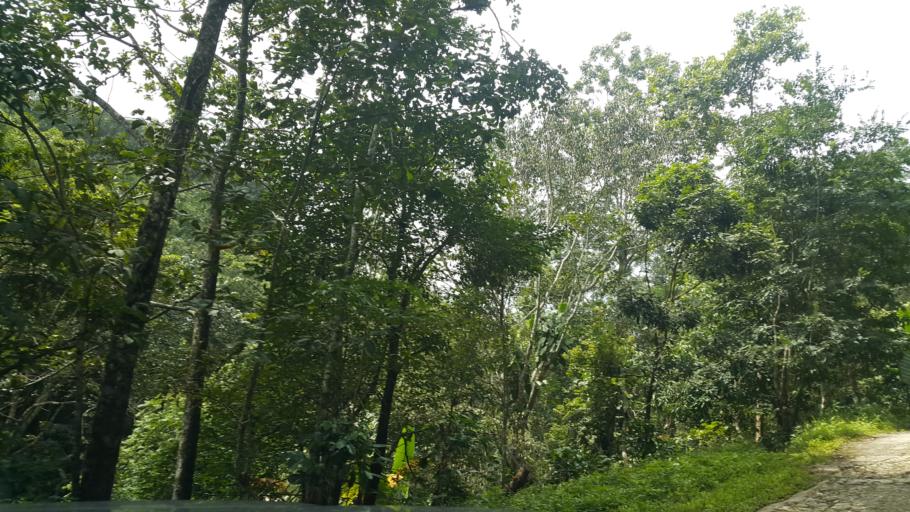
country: TH
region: Lampang
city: Wang Nuea
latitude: 19.0945
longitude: 99.3697
